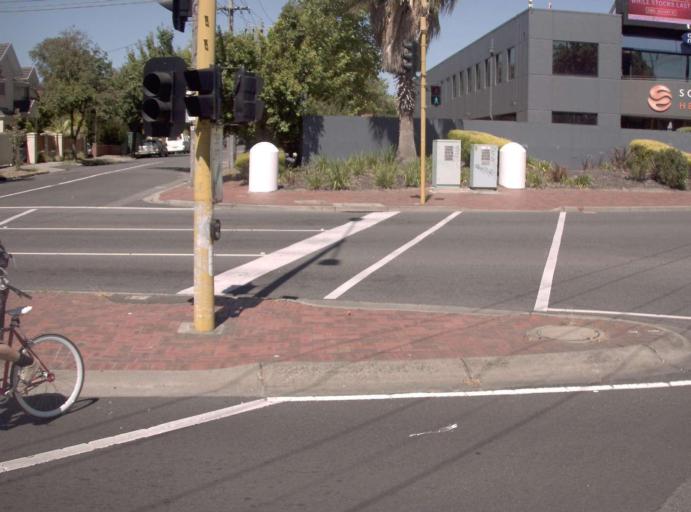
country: AU
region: Victoria
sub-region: Stonnington
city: Malvern East
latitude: -37.8735
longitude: 145.0382
